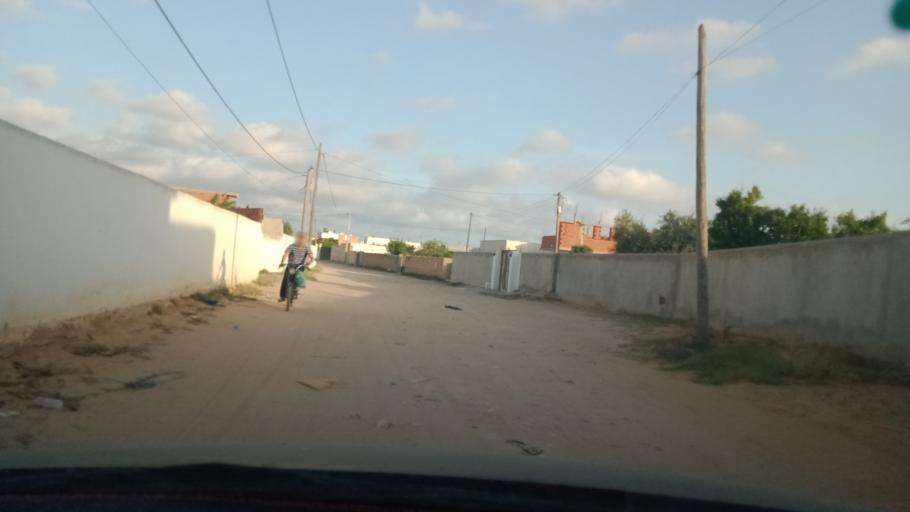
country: TN
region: Safaqis
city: Al Qarmadah
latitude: 34.8174
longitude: 10.7471
